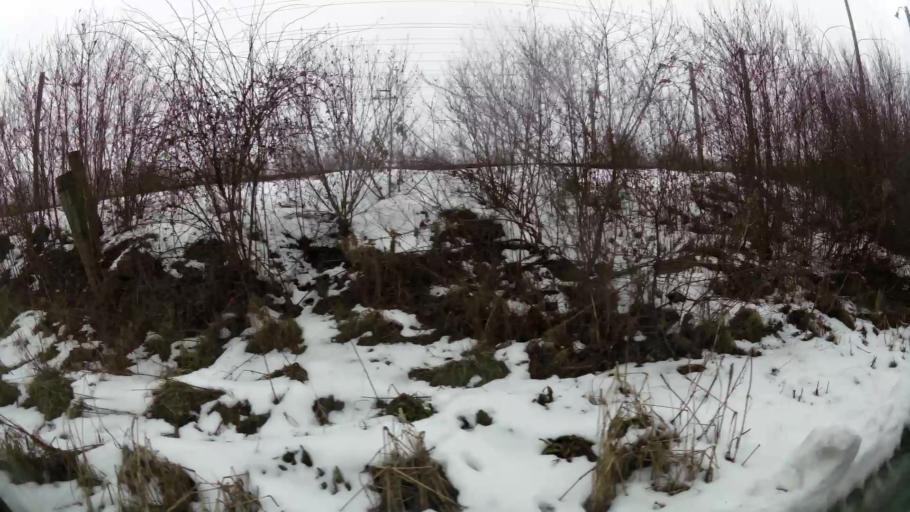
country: RO
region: Ilfov
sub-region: Comuna Chitila
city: Rudeni
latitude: 44.4674
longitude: 25.9767
